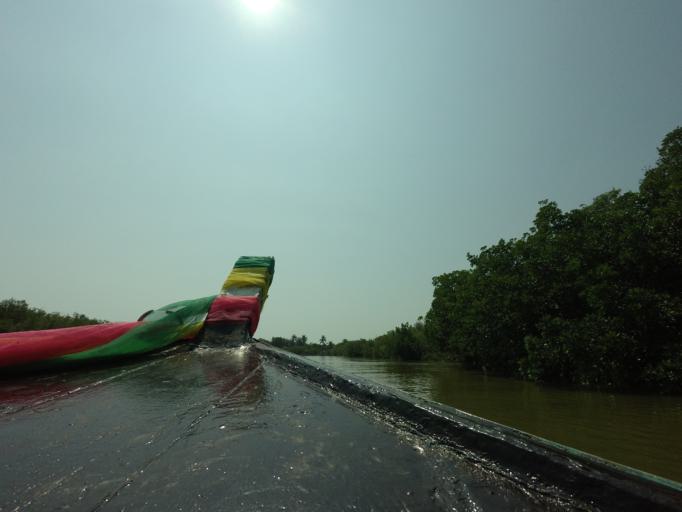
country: TH
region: Prachuap Khiri Khan
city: Kui Buri
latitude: 12.1357
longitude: 99.9674
